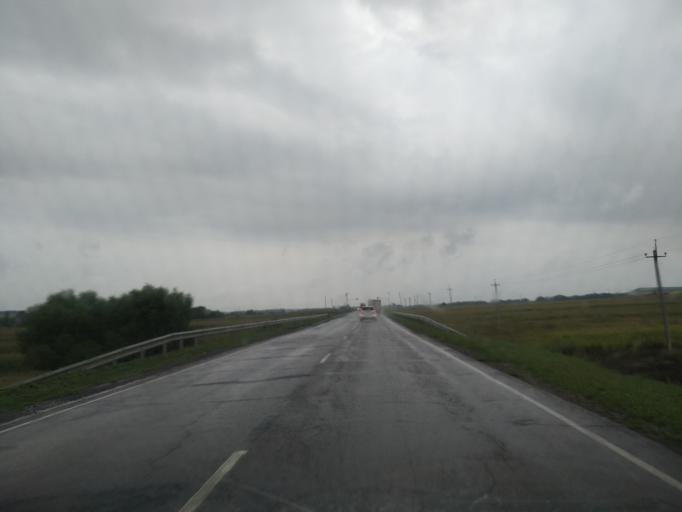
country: RU
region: Voronezj
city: Verkhnyaya Khava
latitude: 51.6780
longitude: 39.8706
